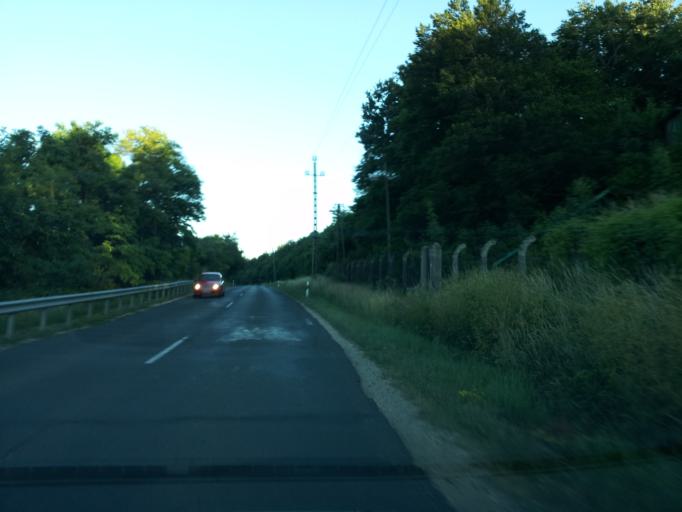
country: HU
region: Veszprem
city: Zirc
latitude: 47.1916
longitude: 17.9218
